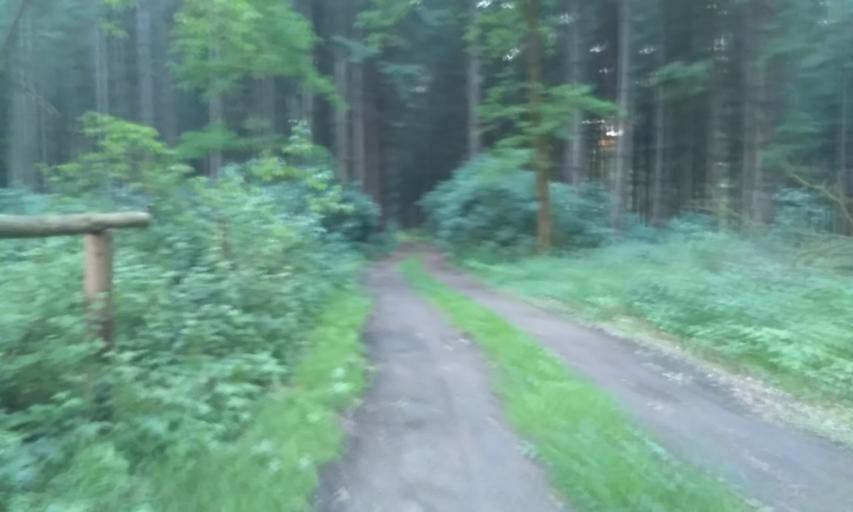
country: DE
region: Lower Saxony
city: Dollern
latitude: 53.5268
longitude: 9.5290
